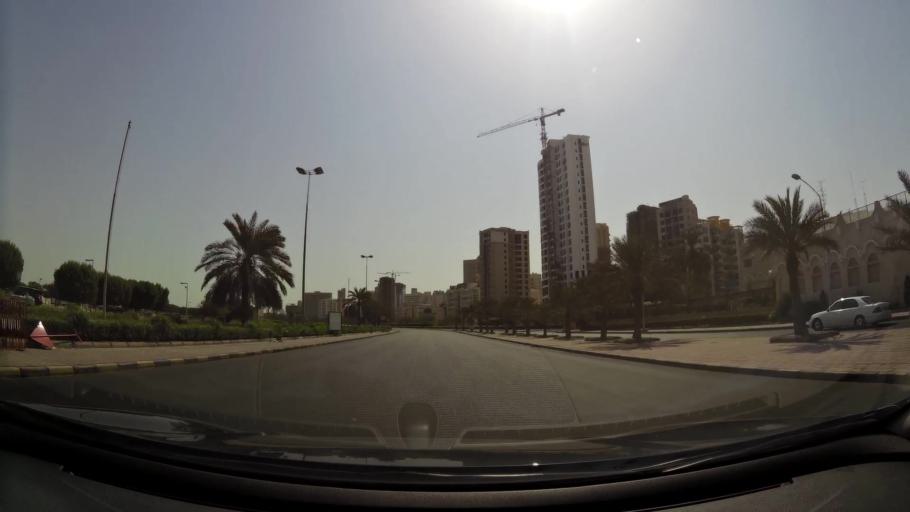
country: KW
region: Al Asimah
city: Ad Dasmah
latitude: 29.3760
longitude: 48.0045
